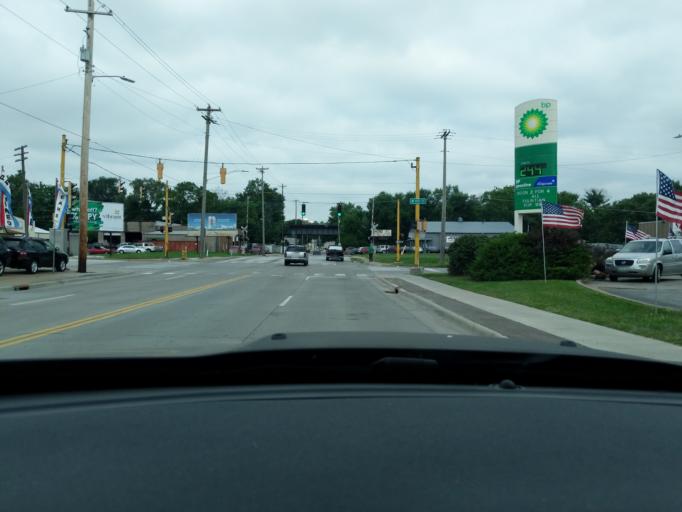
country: US
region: Iowa
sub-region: Scott County
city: Davenport
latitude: 41.5231
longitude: -90.6012
